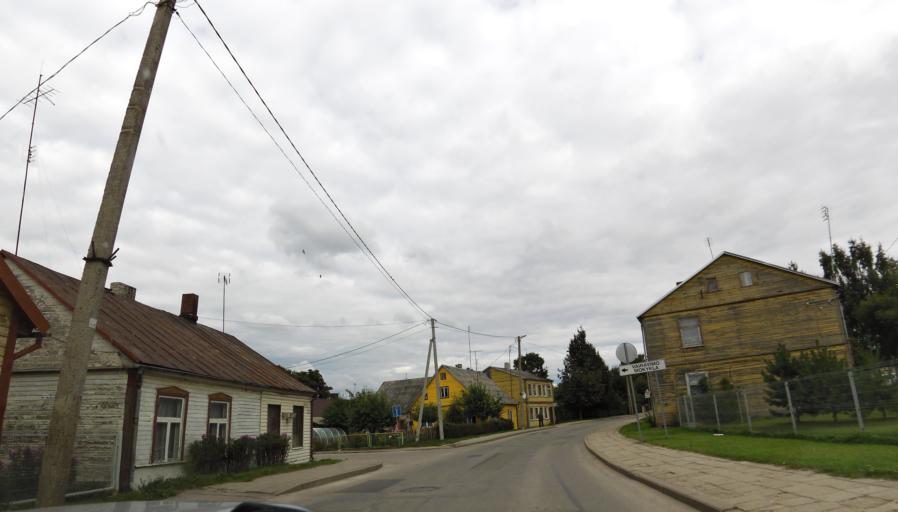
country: LT
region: Panevezys
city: Pasvalys
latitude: 56.0629
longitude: 24.4025
